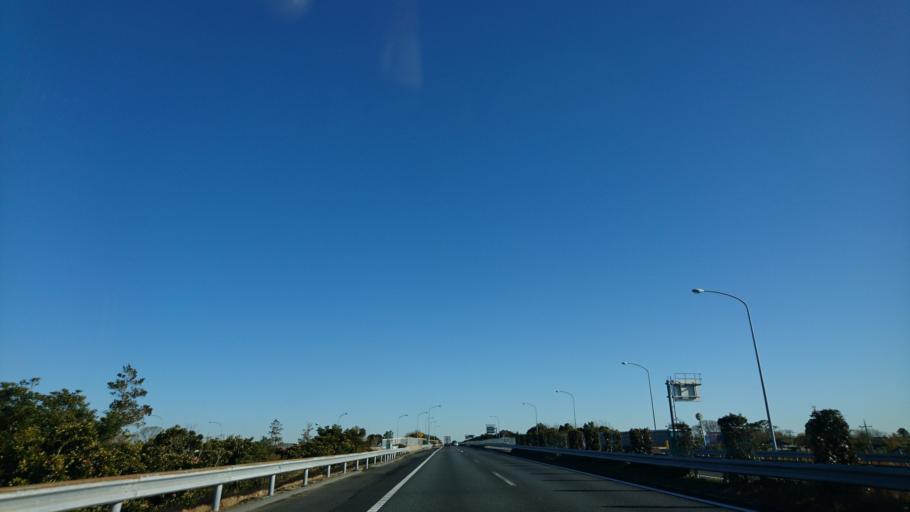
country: JP
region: Chiba
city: Ichihara
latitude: 35.4956
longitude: 140.0927
